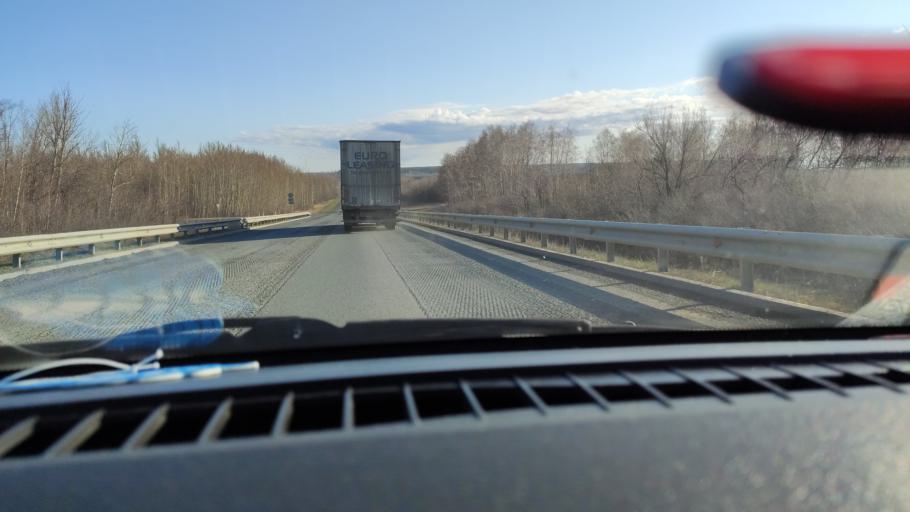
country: RU
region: Saratov
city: Dukhovnitskoye
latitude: 52.6914
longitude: 48.2443
